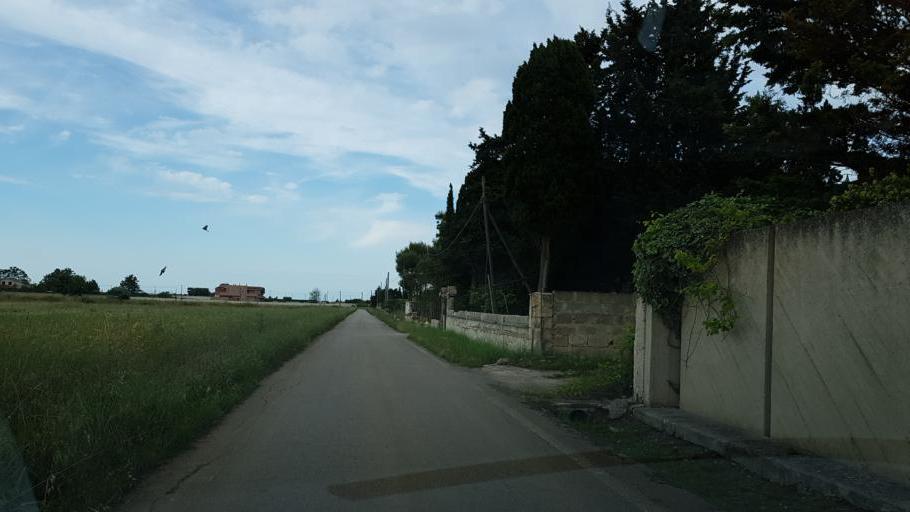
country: IT
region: Apulia
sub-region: Provincia di Brindisi
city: Materdomini
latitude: 40.6598
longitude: 17.9352
